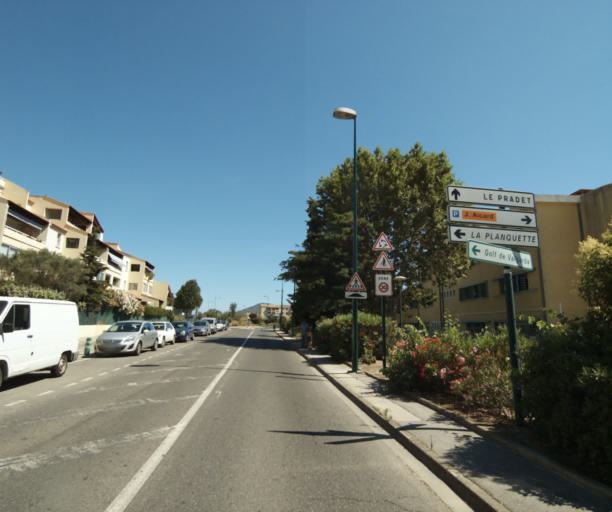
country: FR
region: Provence-Alpes-Cote d'Azur
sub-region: Departement du Var
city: La Garde
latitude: 43.1262
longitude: 6.0157
